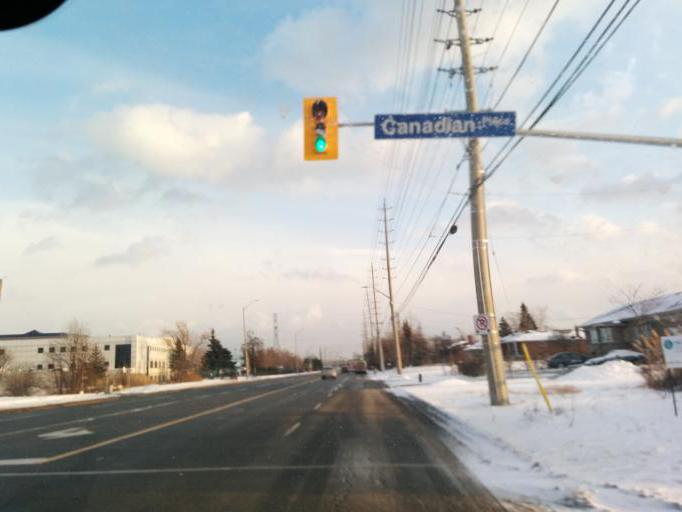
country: CA
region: Ontario
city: Mississauga
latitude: 43.6257
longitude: -79.6284
